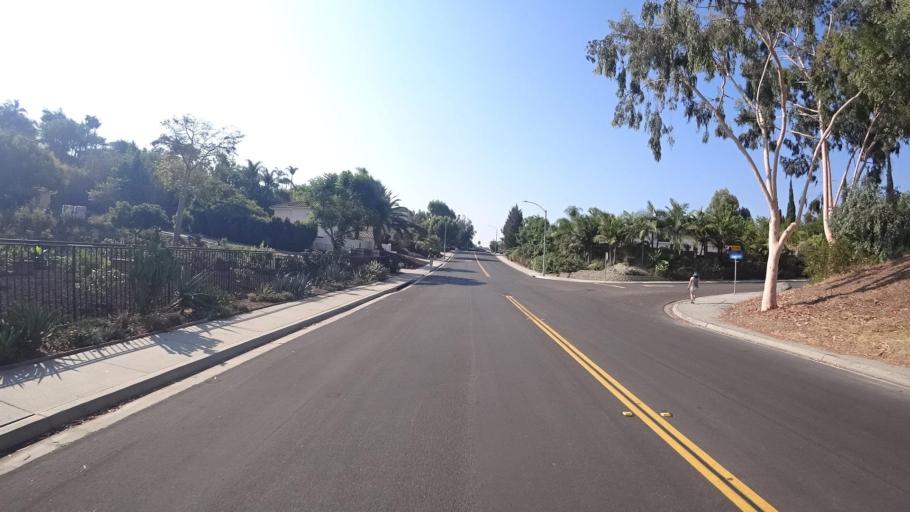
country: US
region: California
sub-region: San Diego County
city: Vista
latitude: 33.2306
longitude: -117.2430
